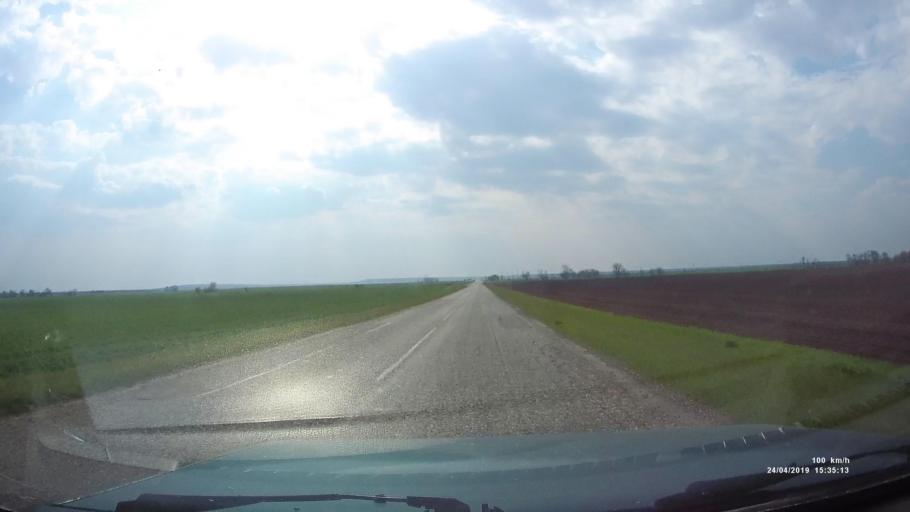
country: RU
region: Kalmykiya
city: Yashalta
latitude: 46.5994
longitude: 42.8987
